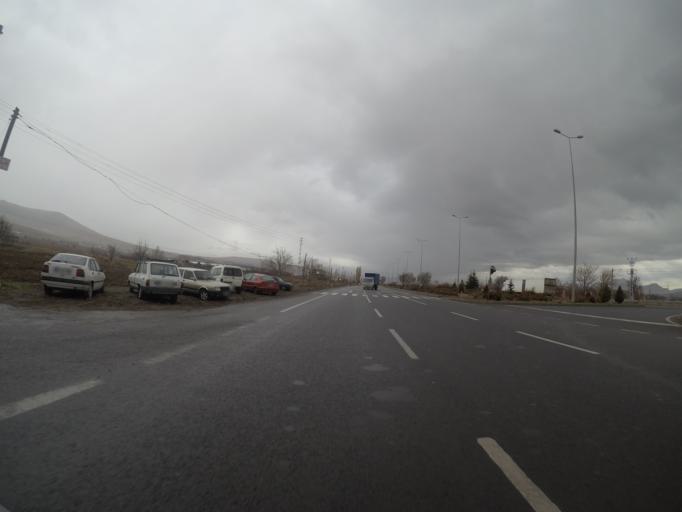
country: TR
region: Kayseri
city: Incesu
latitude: 38.6968
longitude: 35.2486
